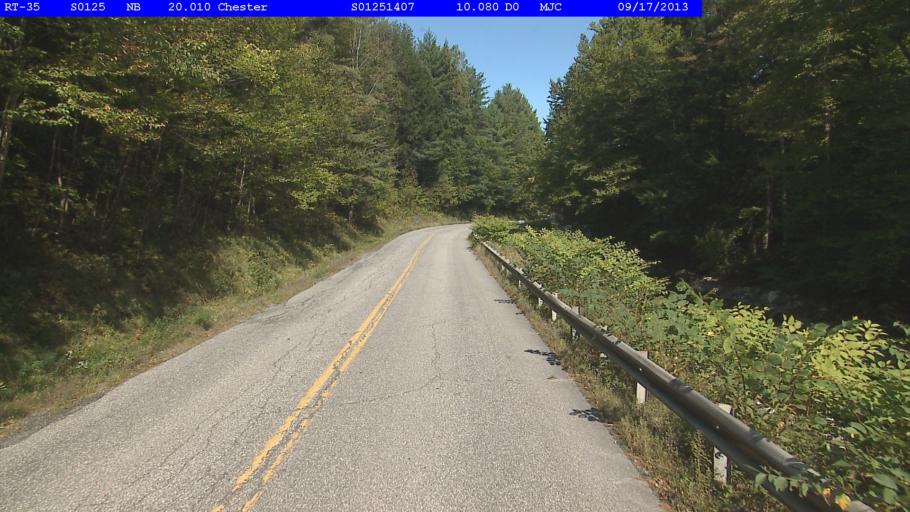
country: US
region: Vermont
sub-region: Windsor County
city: Chester
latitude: 43.2486
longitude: -72.6035
